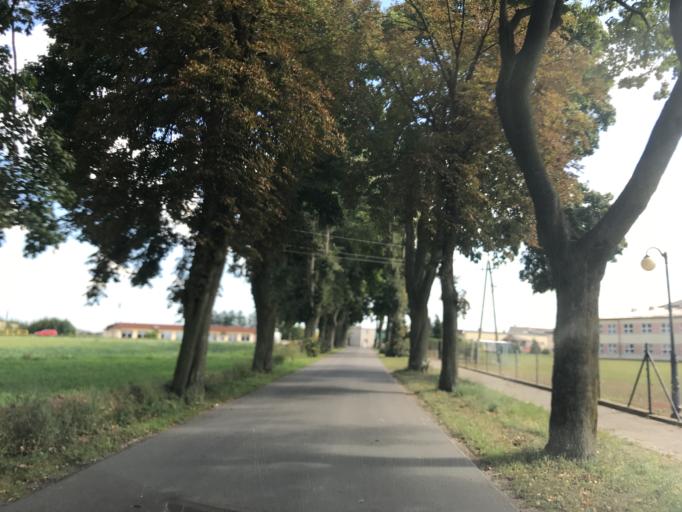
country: PL
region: Kujawsko-Pomorskie
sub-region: Powiat brodnicki
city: Brzozie
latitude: 53.3546
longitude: 19.6996
